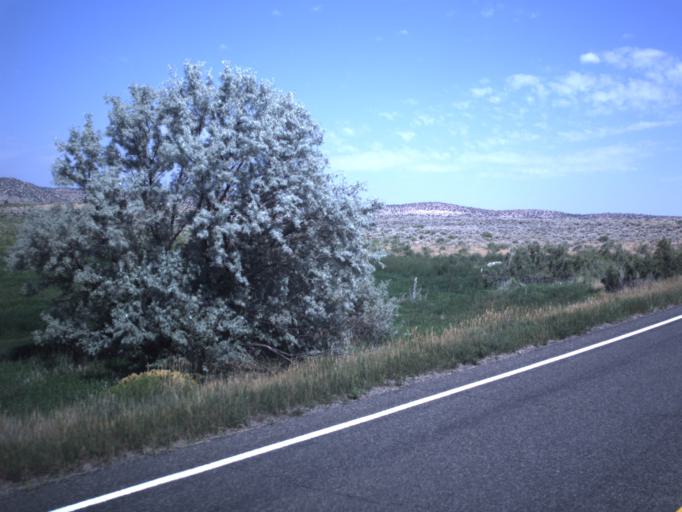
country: US
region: Utah
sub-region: Daggett County
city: Manila
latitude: 40.9674
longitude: -109.7131
